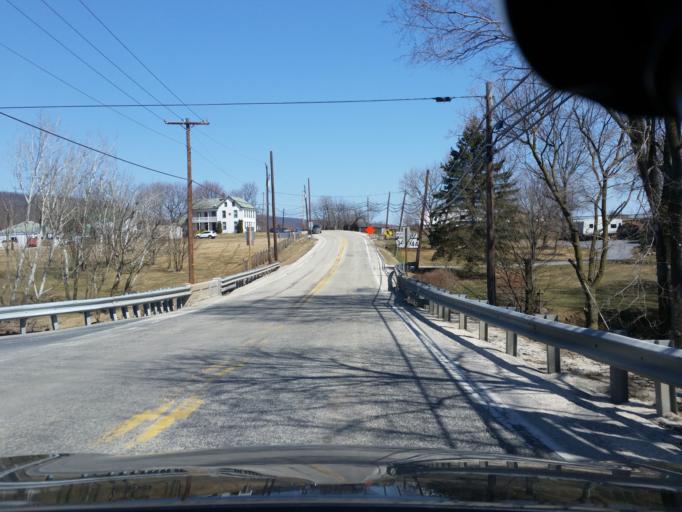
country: US
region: Pennsylvania
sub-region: Cumberland County
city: Schlusser
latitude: 40.2682
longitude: -77.1670
